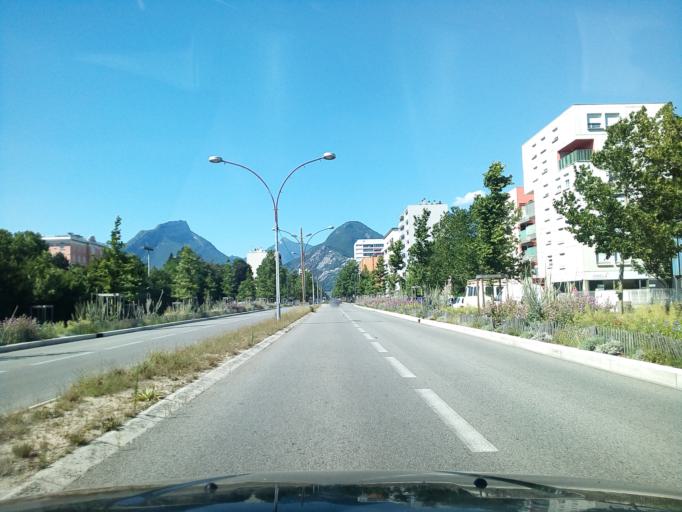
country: FR
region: Rhone-Alpes
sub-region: Departement de l'Isere
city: Grenoble
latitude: 45.1656
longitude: 5.7115
